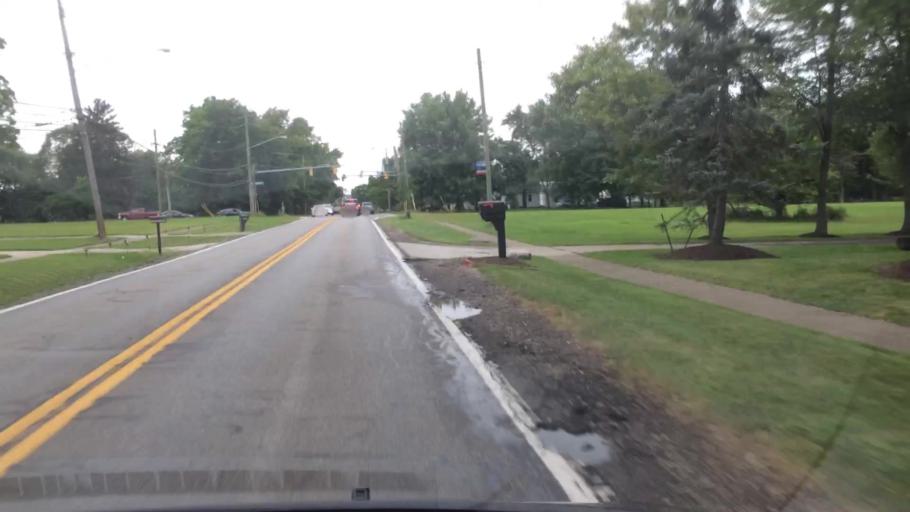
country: US
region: Ohio
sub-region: Cuyahoga County
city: Strongsville
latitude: 41.3007
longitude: -81.8110
